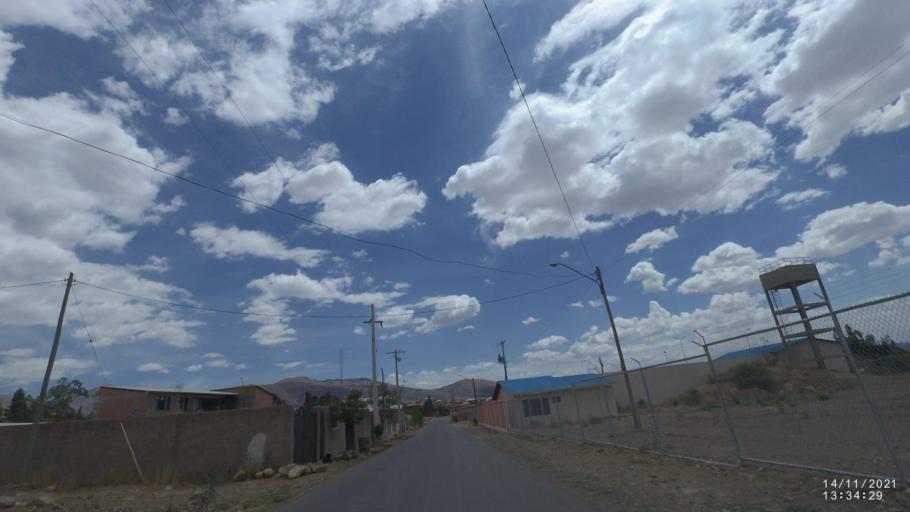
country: BO
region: Cochabamba
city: Colomi
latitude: -17.4027
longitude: -65.9845
